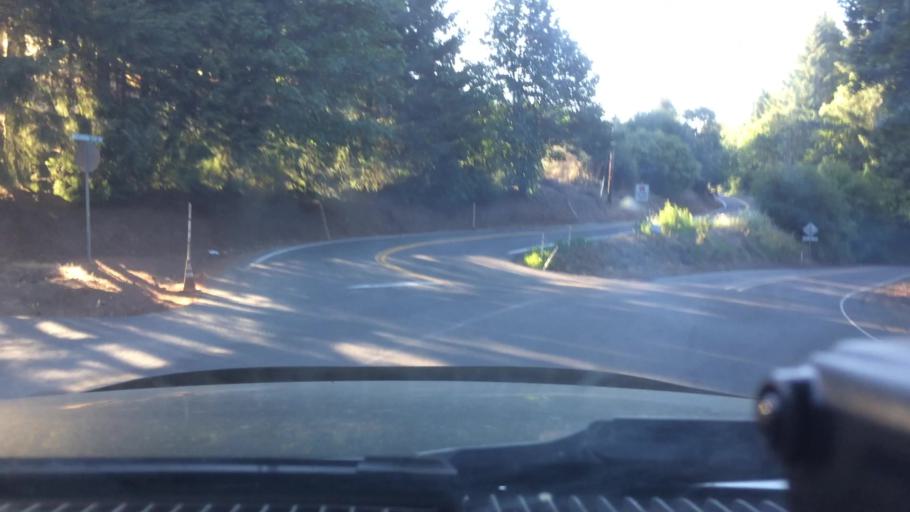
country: US
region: Oregon
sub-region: Yamhill County
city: Newberg
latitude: 45.3464
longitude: -122.9628
